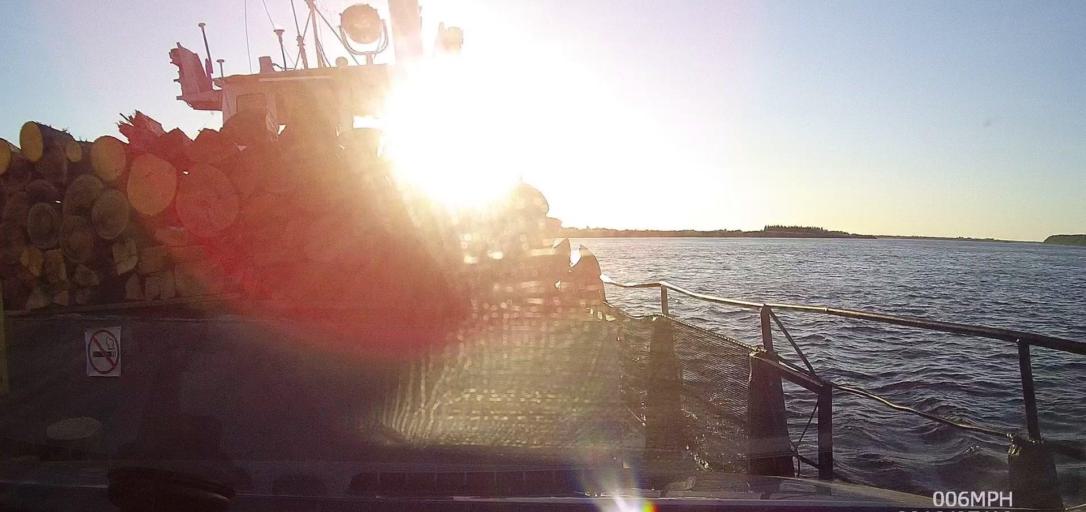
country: RU
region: Arkhangelskaya
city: Lukovetskiy
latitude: 64.1580
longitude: 41.9170
